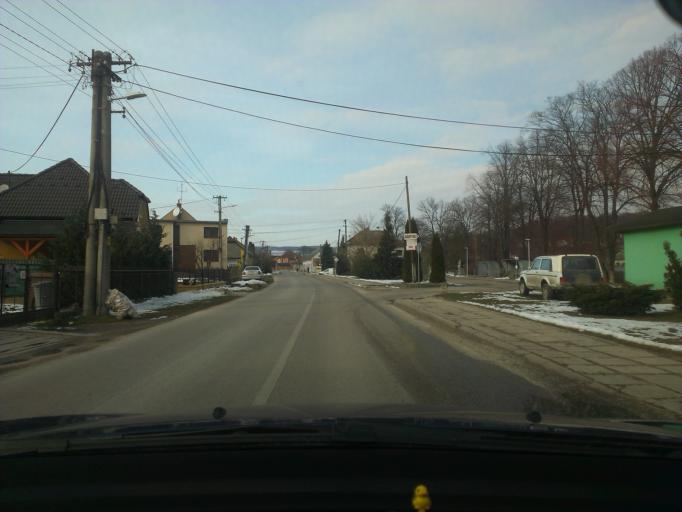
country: SK
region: Nitriansky
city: Stara Tura
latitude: 48.7003
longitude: 17.6863
